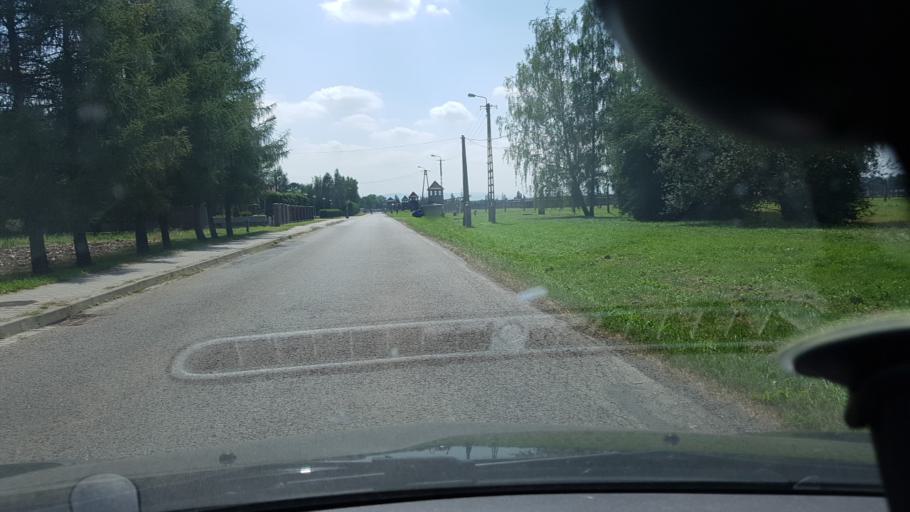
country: PL
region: Lesser Poland Voivodeship
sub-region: Powiat oswiecimski
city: Brzezinka
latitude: 50.0416
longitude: 19.1814
